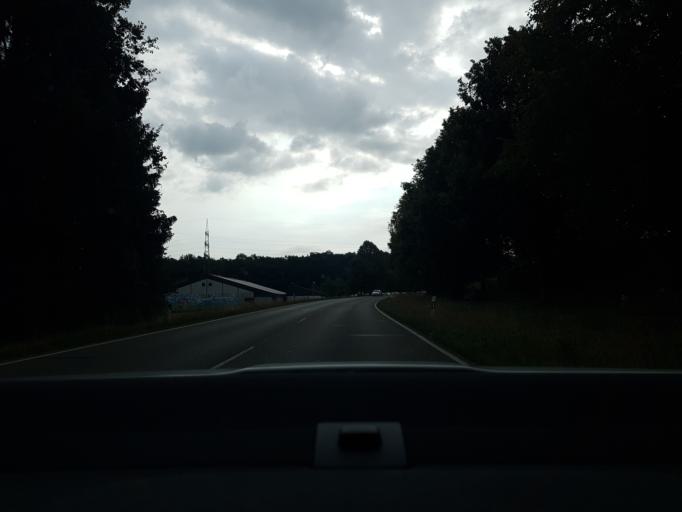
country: DE
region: Hesse
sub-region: Regierungsbezirk Giessen
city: Limburg an der Lahn
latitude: 50.3757
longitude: 8.0777
